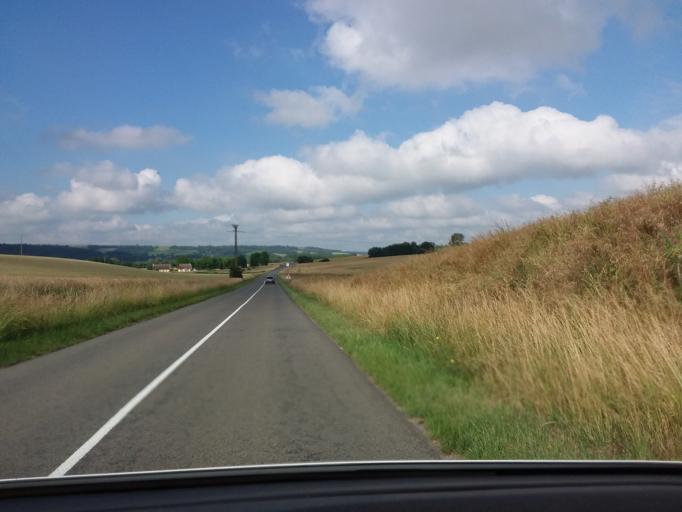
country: FR
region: Champagne-Ardenne
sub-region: Departement de la Marne
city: Jonchery-sur-Vesle
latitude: 49.3914
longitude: 3.7740
